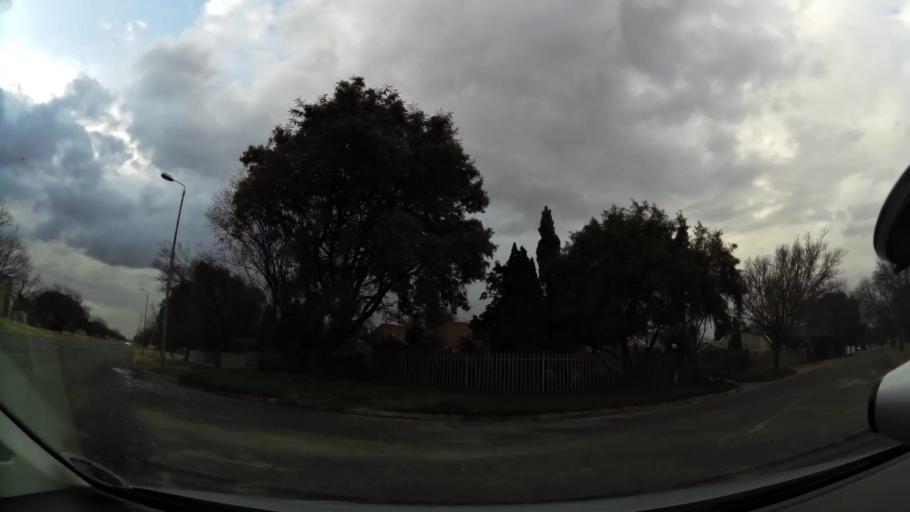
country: ZA
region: Orange Free State
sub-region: Lejweleputswa District Municipality
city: Welkom
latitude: -27.9515
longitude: 26.7252
